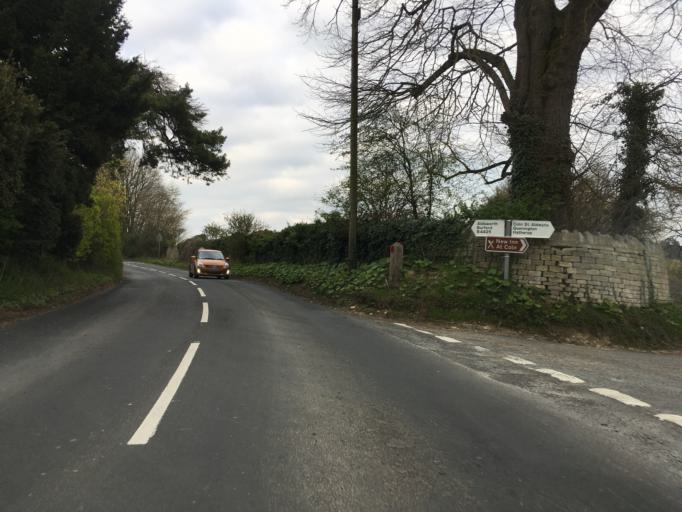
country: GB
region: England
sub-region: Gloucestershire
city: Fairford
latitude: 51.7592
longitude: -1.8298
